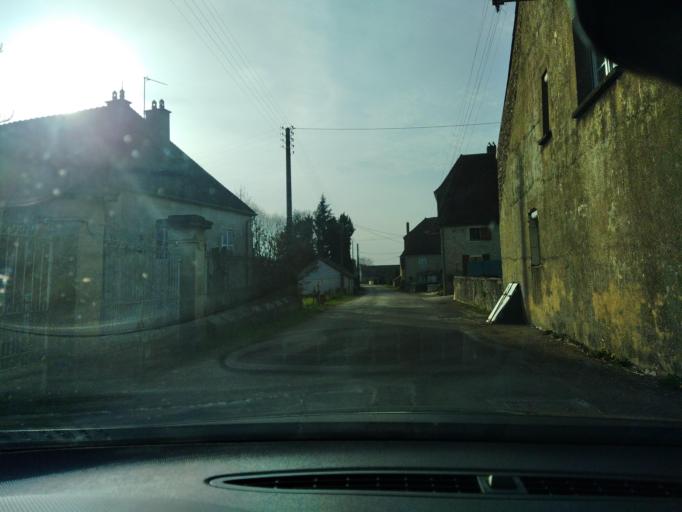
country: FR
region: Franche-Comte
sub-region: Departement du Jura
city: Chaussin
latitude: 46.9887
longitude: 5.4575
